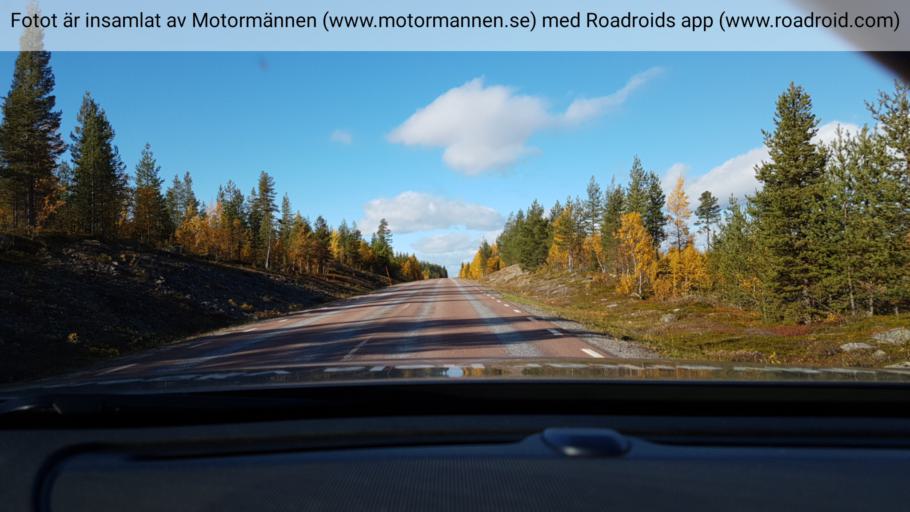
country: SE
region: Norrbotten
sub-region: Arjeplogs Kommun
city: Arjeplog
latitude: 66.0562
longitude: 17.9855
